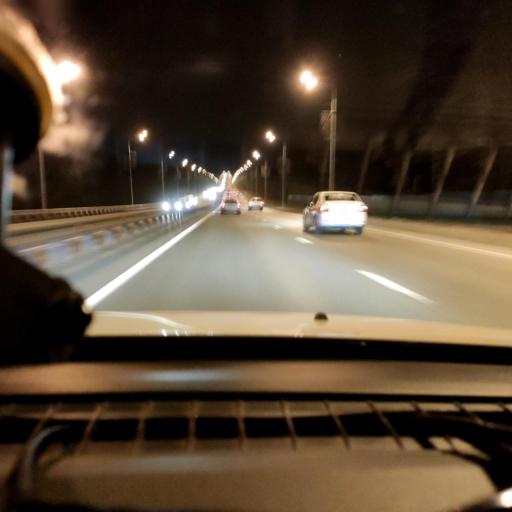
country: RU
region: Samara
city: Novosemeykino
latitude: 53.3402
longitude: 50.2326
